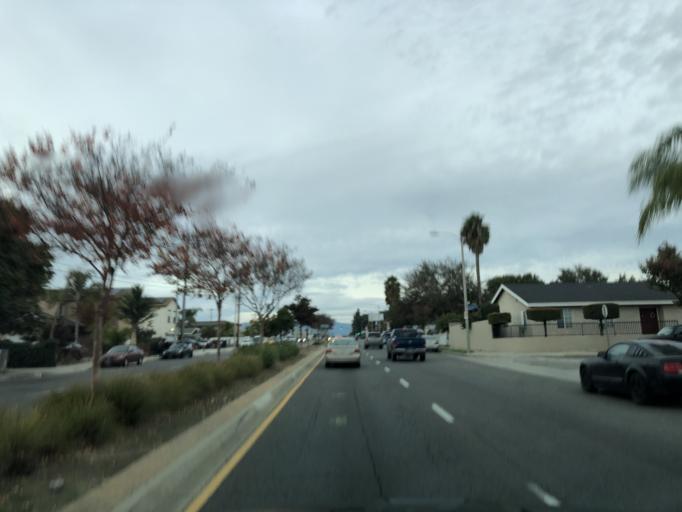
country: US
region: California
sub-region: Los Angeles County
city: La Mirada
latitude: 33.9224
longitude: -118.0465
